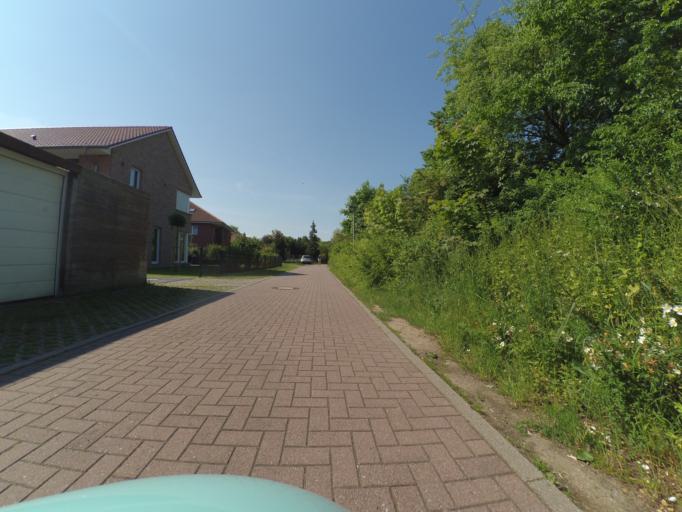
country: DE
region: Lower Saxony
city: Burgdorf
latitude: 52.4480
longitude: 9.9980
